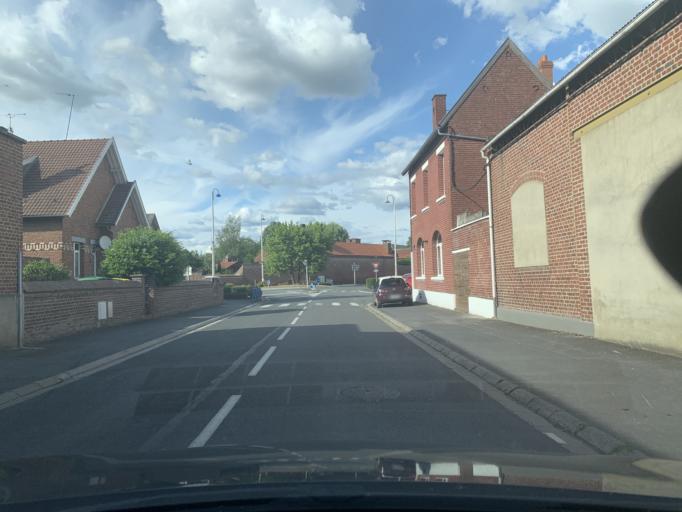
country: FR
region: Nord-Pas-de-Calais
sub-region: Departement du Nord
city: Marcoing
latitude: 50.1212
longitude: 3.1726
